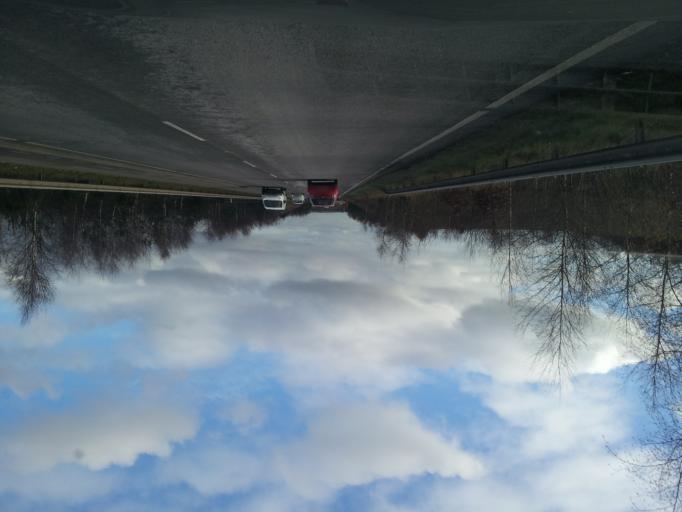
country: GB
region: England
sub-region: Nottinghamshire
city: Mansfield
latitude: 53.1213
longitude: -1.2072
